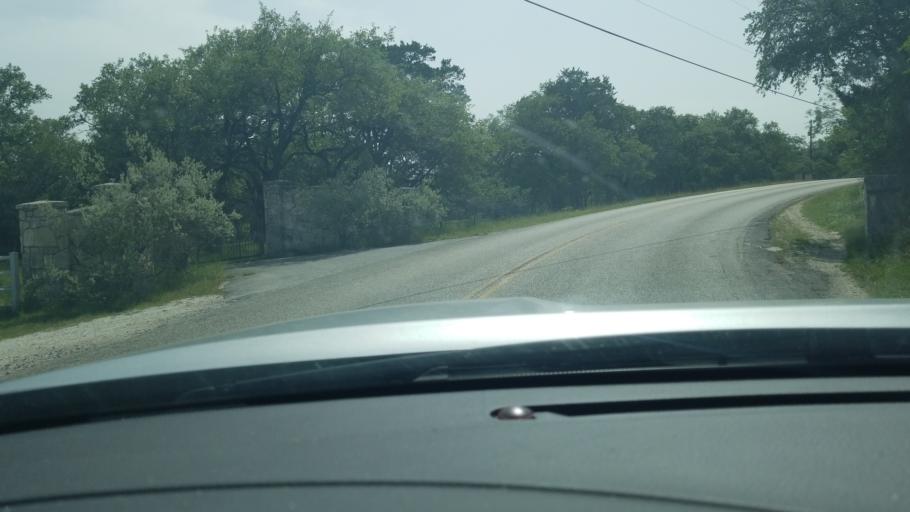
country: US
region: Texas
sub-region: Comal County
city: Bulverde
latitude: 29.7934
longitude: -98.4388
